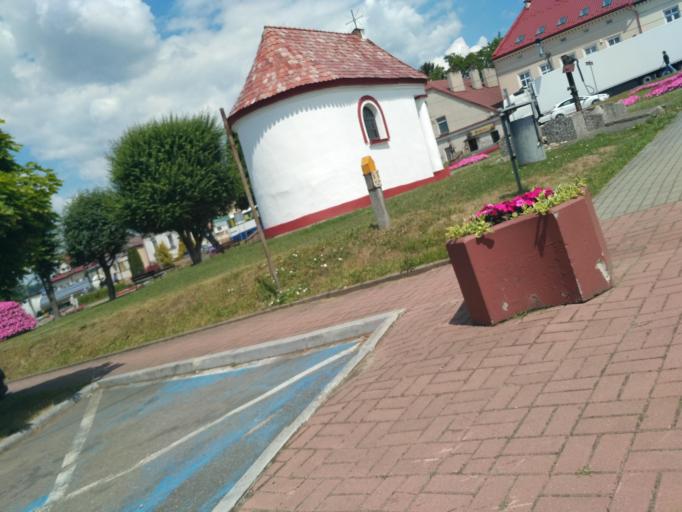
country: PL
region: Subcarpathian Voivodeship
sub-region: Powiat debicki
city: Brzostek
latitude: 49.8789
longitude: 21.4110
